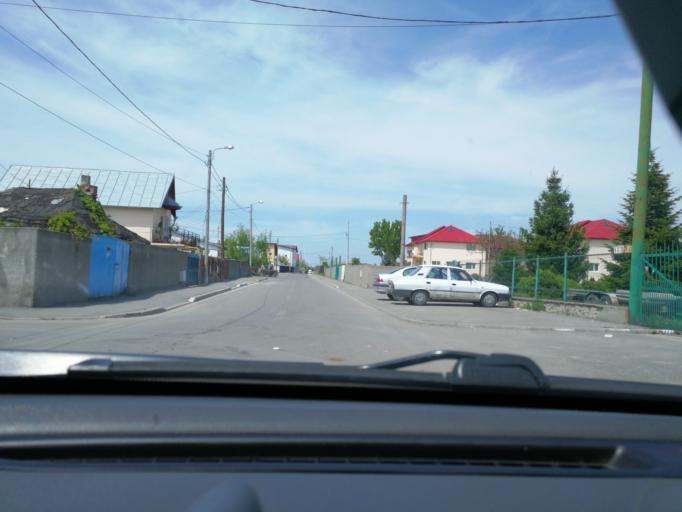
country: RO
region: Prahova
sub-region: Comuna Bucov
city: Bucov
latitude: 44.9496
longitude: 26.0526
